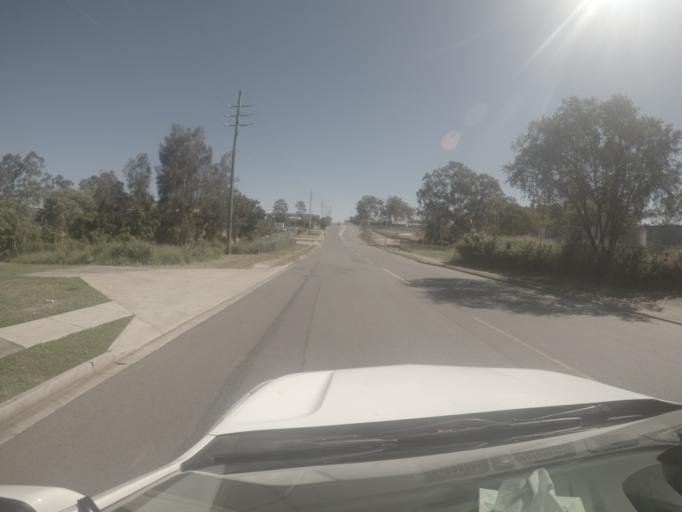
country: AU
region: Queensland
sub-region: Brisbane
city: Wacol
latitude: -27.5826
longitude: 152.9457
